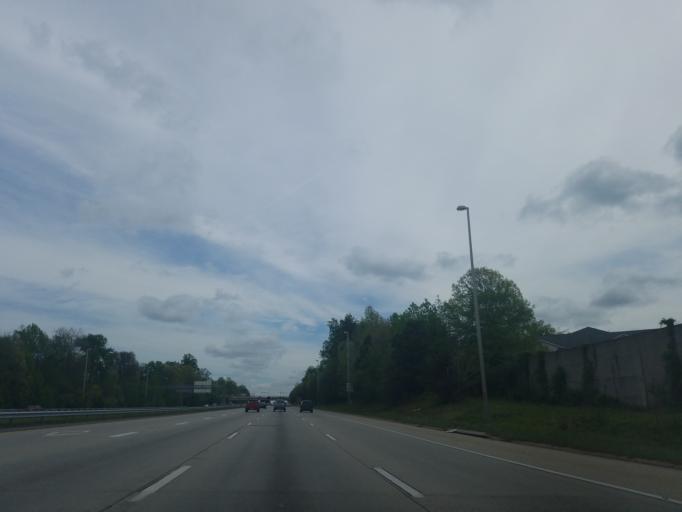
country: US
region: Virginia
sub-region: Fairfax County
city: Greenbriar
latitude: 38.8575
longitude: -77.3712
